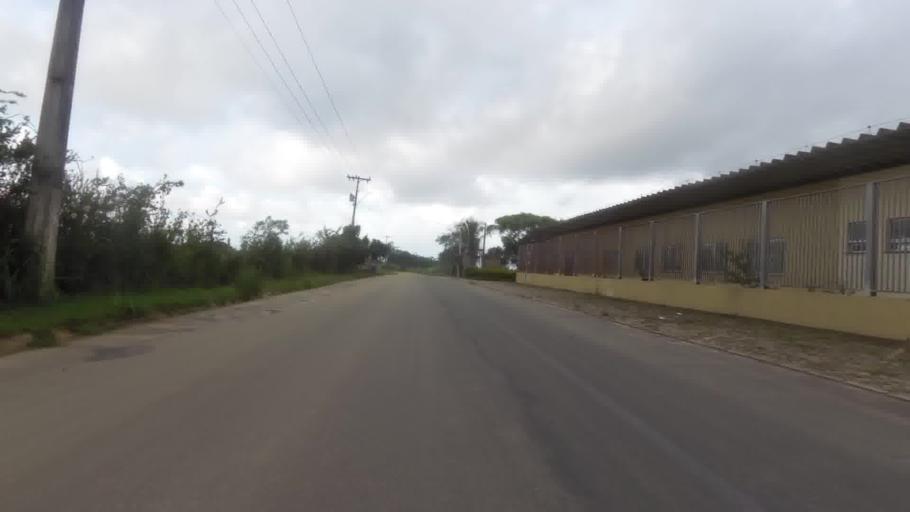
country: BR
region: Espirito Santo
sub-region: Piuma
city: Piuma
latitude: -20.7725
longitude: -40.6303
